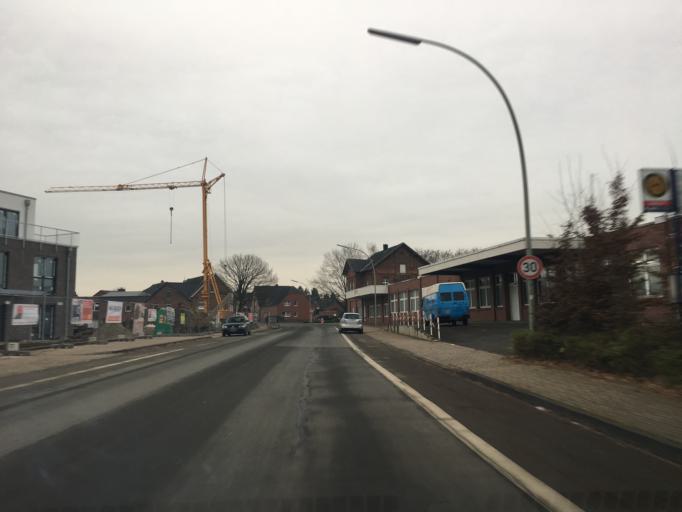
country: DE
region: North Rhine-Westphalia
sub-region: Regierungsbezirk Munster
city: Nordkirchen
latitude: 51.7412
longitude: 7.5185
